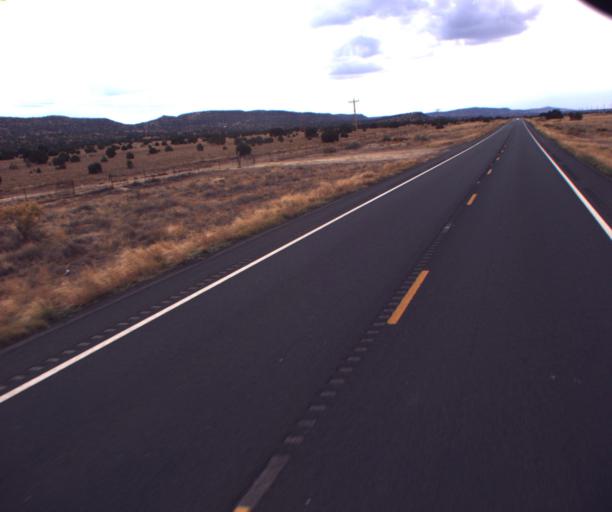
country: US
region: Arizona
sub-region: Navajo County
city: Kayenta
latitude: 36.4890
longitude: -110.6351
